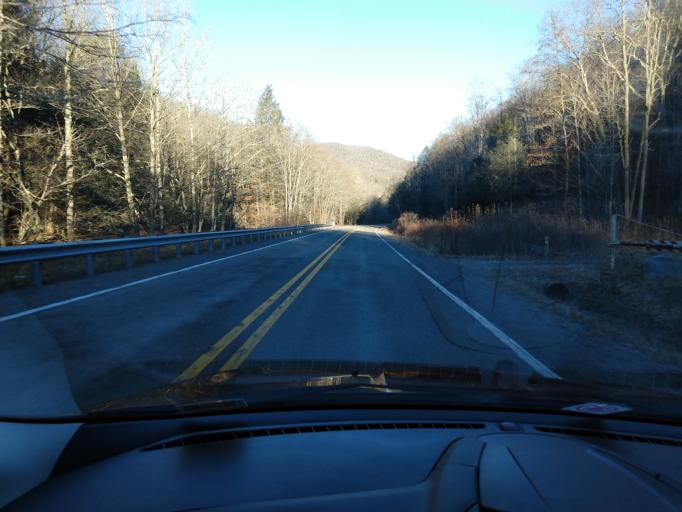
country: US
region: Virginia
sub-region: Highland County
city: Monterey
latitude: 38.5161
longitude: -79.7241
